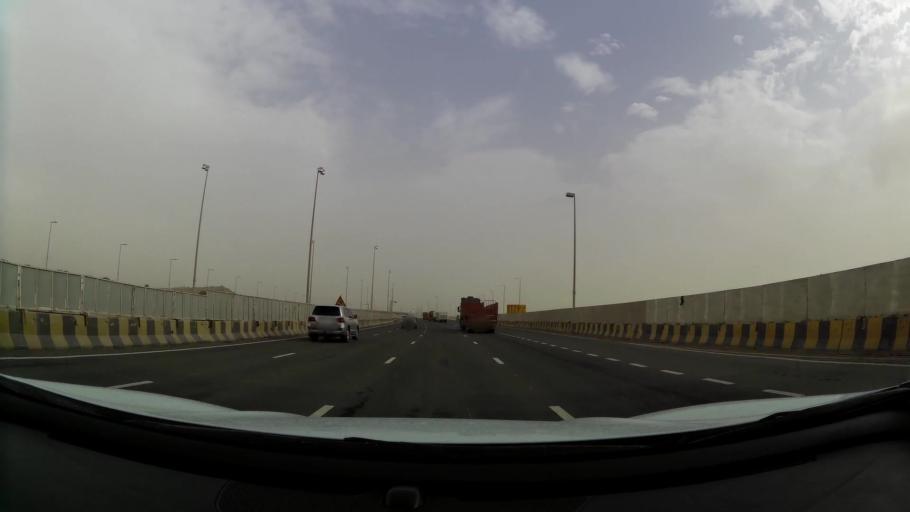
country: AE
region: Abu Dhabi
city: Abu Dhabi
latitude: 24.4587
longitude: 54.6271
